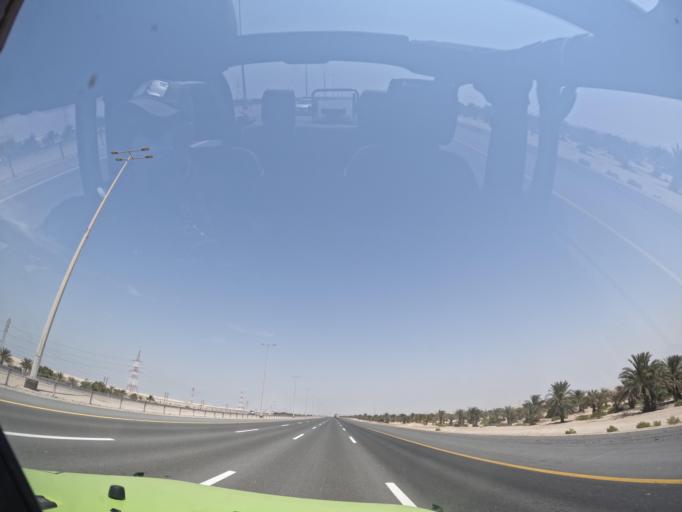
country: AE
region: Abu Dhabi
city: Abu Dhabi
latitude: 24.1950
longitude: 54.3914
